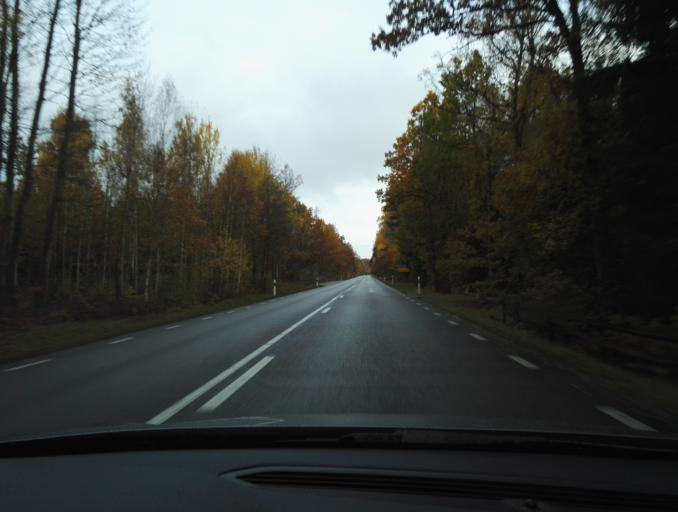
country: SE
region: Kronoberg
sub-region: Vaxjo Kommun
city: Gemla
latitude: 56.9589
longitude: 14.7146
